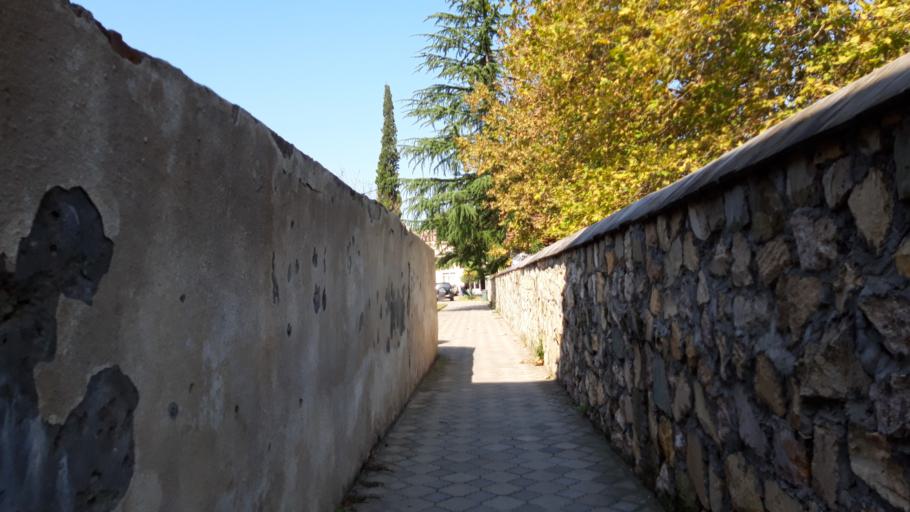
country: GE
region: Imereti
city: Samtredia
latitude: 42.1627
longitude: 42.3449
